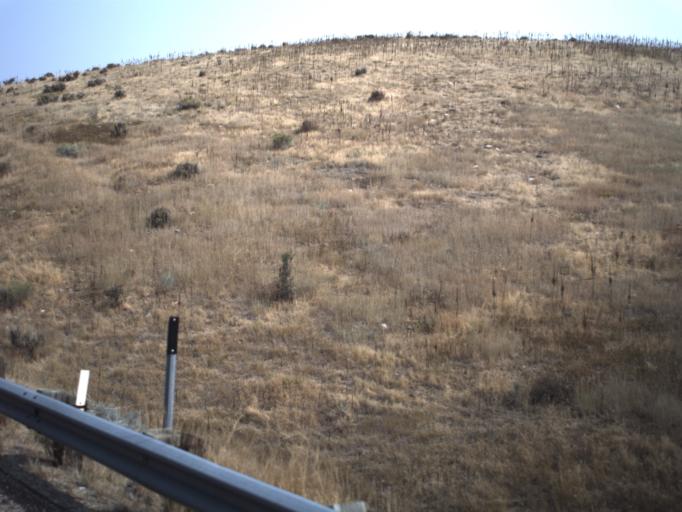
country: US
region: Utah
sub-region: Morgan County
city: Morgan
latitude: 40.9121
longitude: -111.5876
